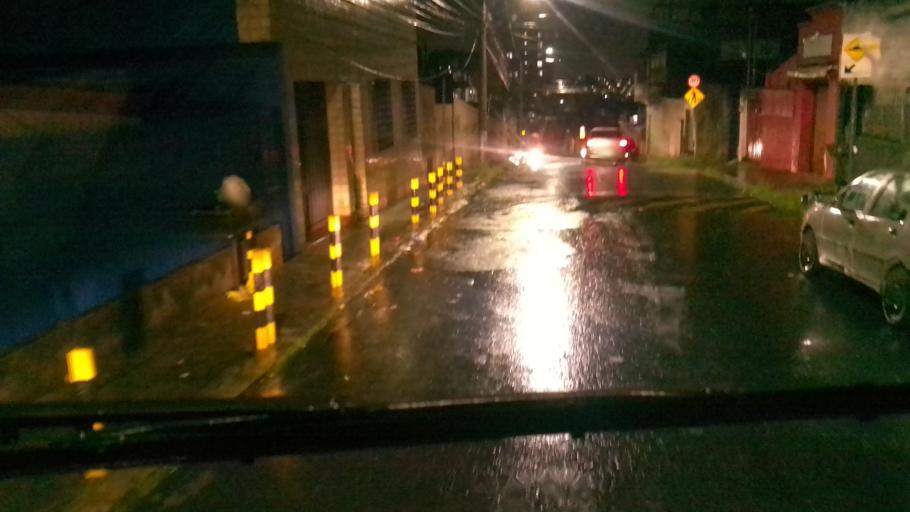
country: BR
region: Minas Gerais
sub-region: Belo Horizonte
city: Belo Horizonte
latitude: -19.8996
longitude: -43.9542
